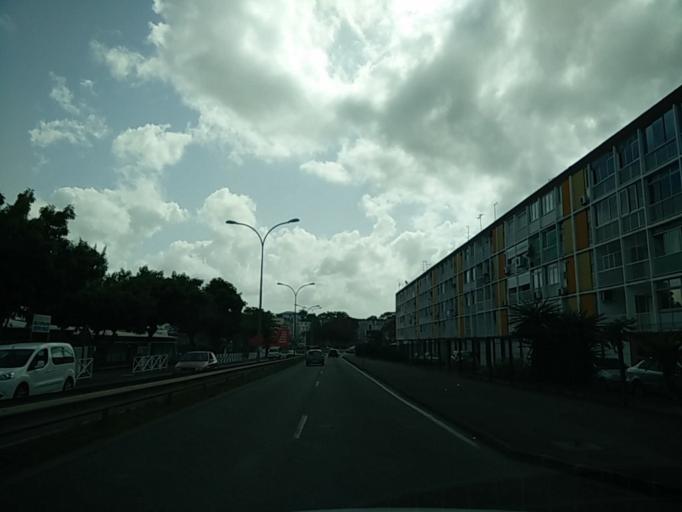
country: GP
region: Guadeloupe
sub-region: Guadeloupe
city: Pointe-a-Pitre
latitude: 16.2507
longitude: -61.5221
